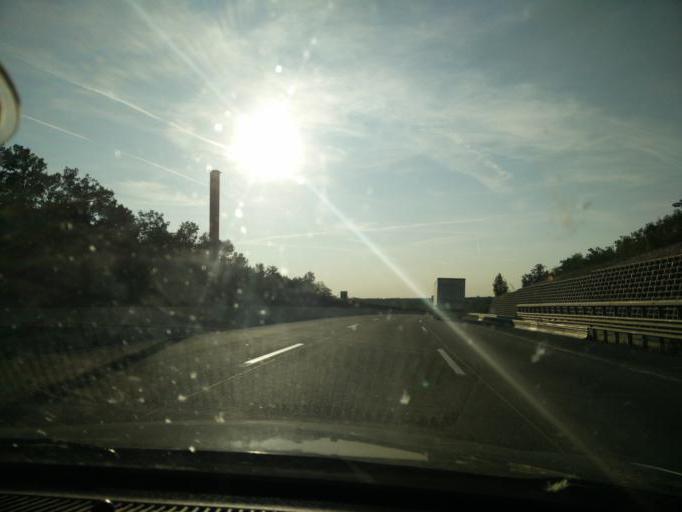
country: HU
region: Pest
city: Toeroekbalint
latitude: 47.4210
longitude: 18.9113
